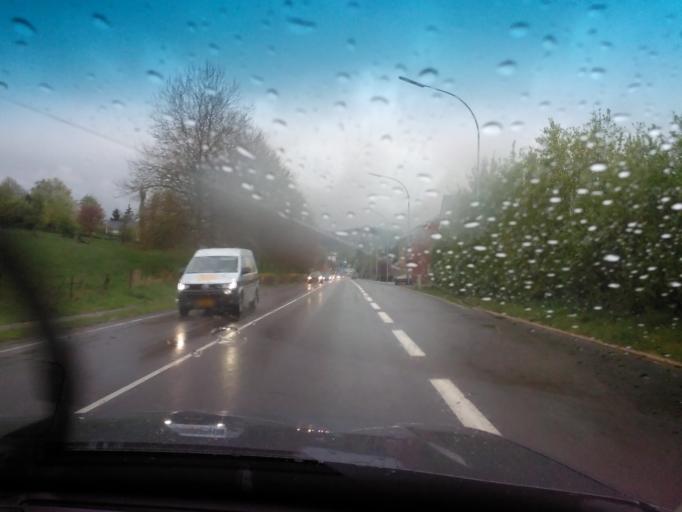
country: LU
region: Grevenmacher
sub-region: Canton de Grevenmacher
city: Junglinster
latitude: 49.7146
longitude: 6.2590
